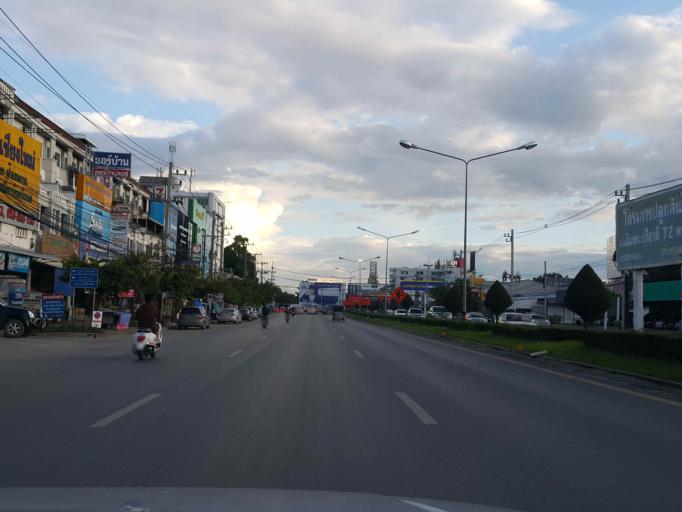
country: TH
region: Chiang Mai
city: Chiang Mai
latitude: 18.8119
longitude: 99.0111
